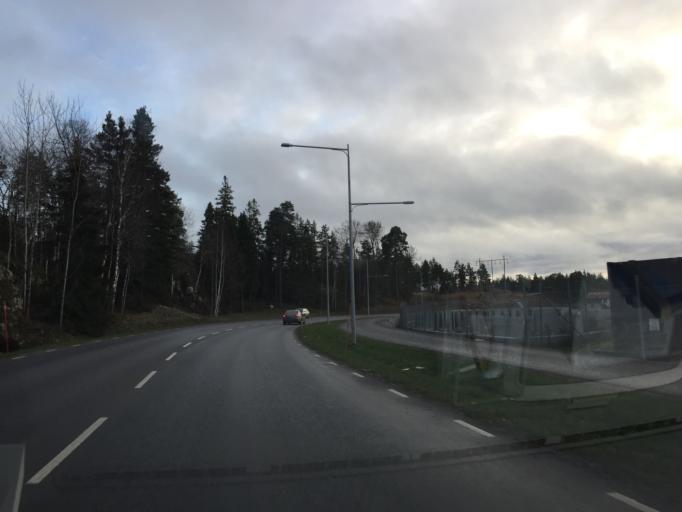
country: SE
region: Stockholm
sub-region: Sodertalje Kommun
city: Soedertaelje
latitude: 59.2169
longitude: 17.6520
